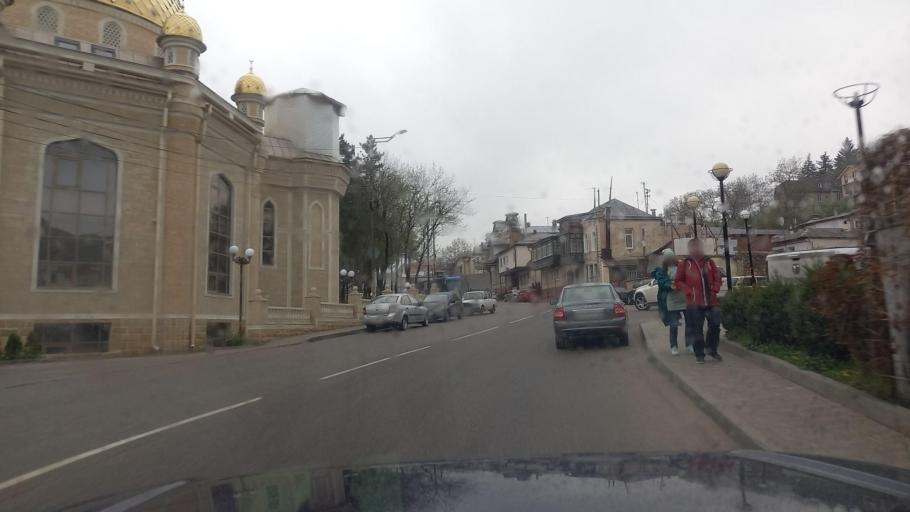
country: RU
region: Stavropol'skiy
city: Kislovodsk
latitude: 43.8947
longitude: 42.7138
